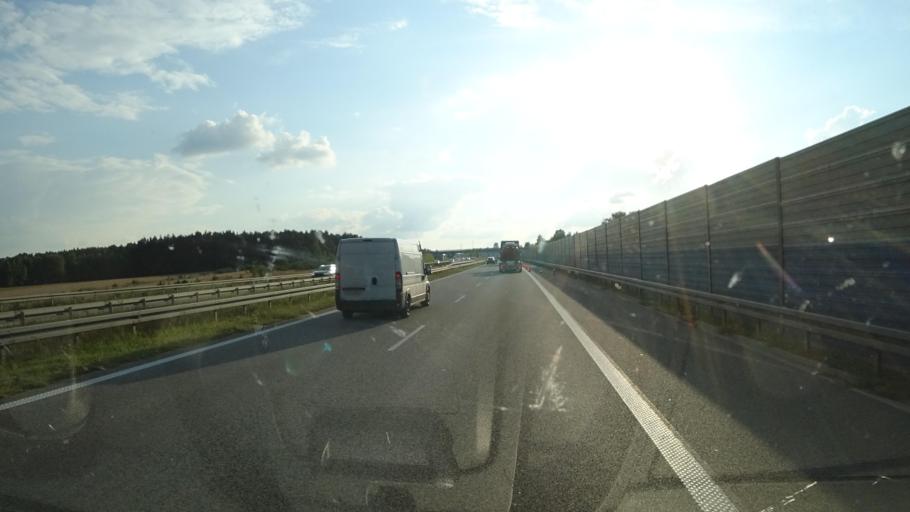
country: PL
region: Lodz Voivodeship
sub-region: Powiat zgierski
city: Strykow
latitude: 51.8969
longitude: 19.6749
